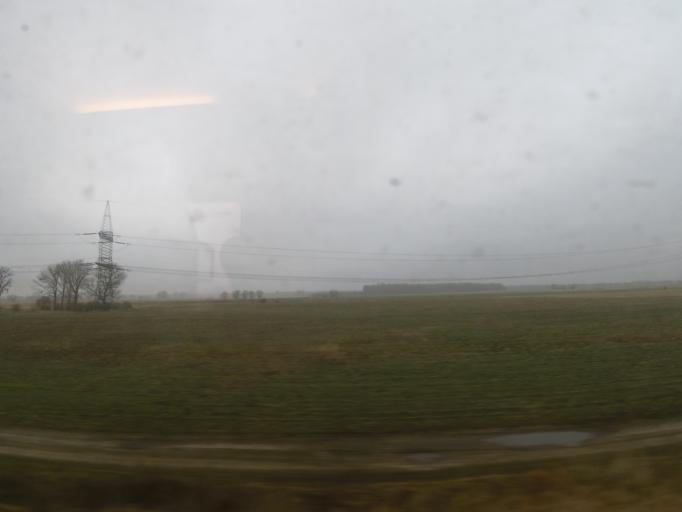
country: DE
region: Brandenburg
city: Wustermark
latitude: 52.5992
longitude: 12.9378
